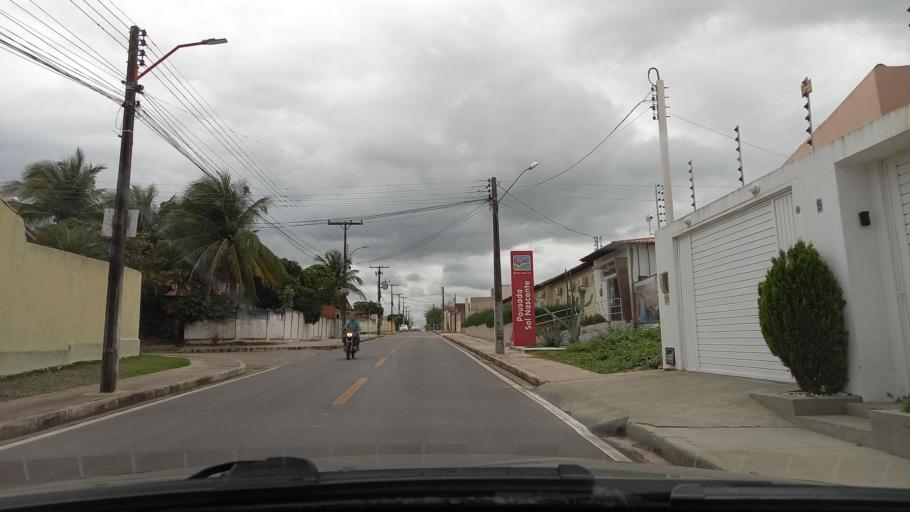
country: BR
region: Sergipe
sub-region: Caninde De Sao Francisco
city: Caninde de Sao Francisco
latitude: -9.6139
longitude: -37.7633
